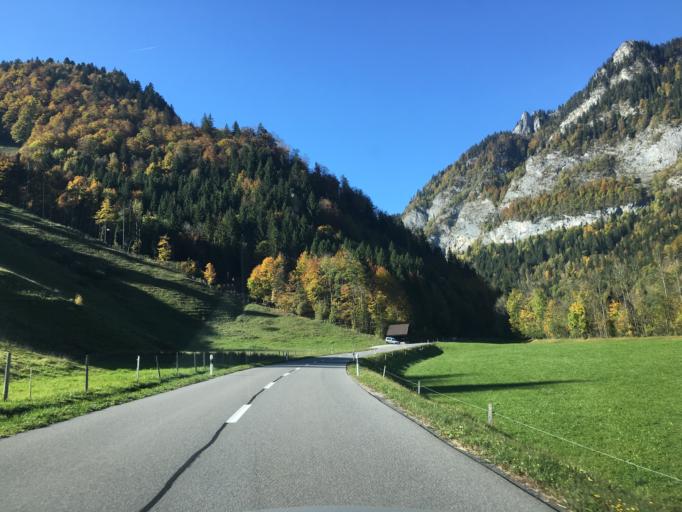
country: CH
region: Fribourg
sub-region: Gruyere District
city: Charmey
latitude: 46.6024
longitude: 7.2021
